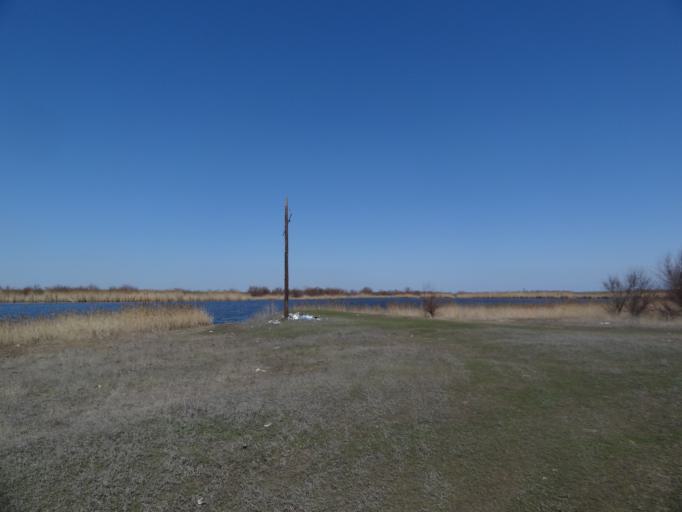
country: RU
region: Saratov
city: Shumeyka
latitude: 51.4220
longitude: 46.3130
